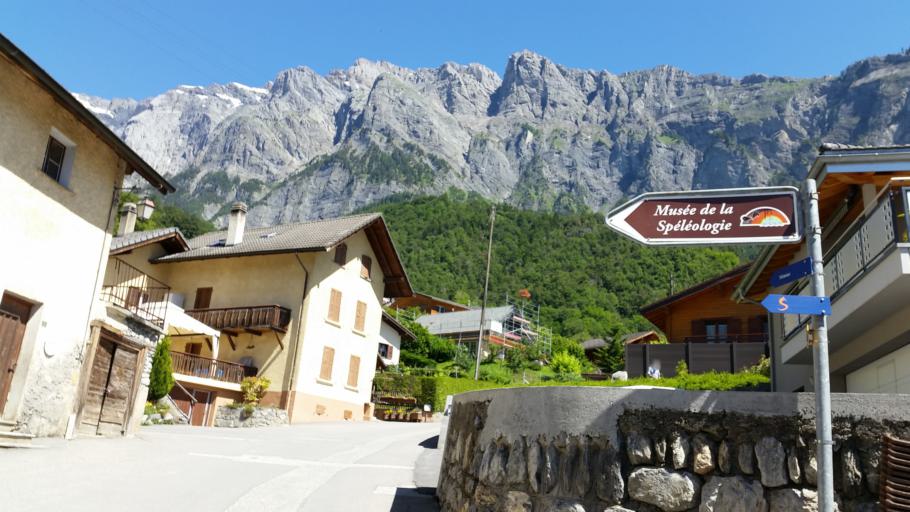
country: CH
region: Valais
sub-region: Conthey District
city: Chamoson
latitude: 46.2081
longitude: 7.2162
